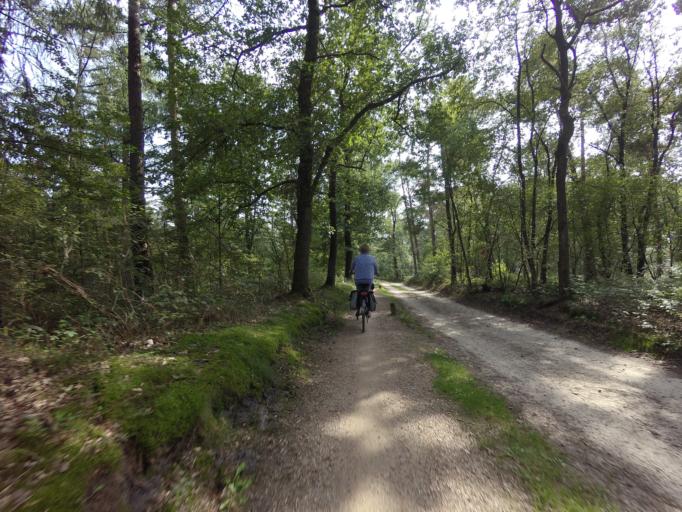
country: DE
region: Lower Saxony
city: Getelo
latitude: 52.4255
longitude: 6.8979
